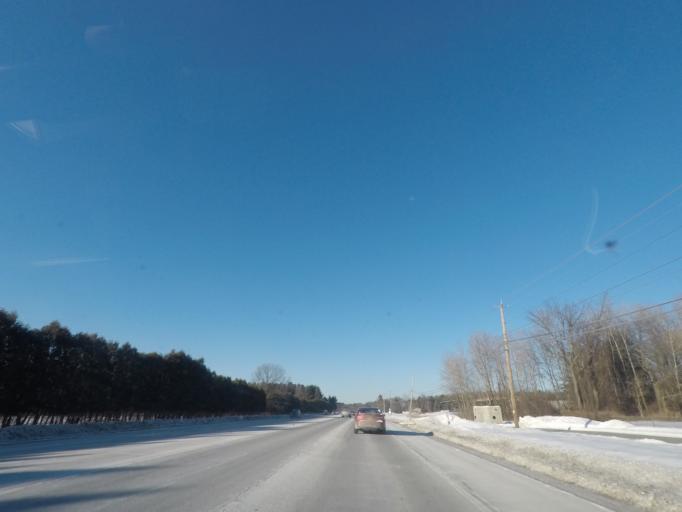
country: US
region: New York
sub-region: Saratoga County
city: Saratoga Springs
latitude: 43.0553
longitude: -73.7879
